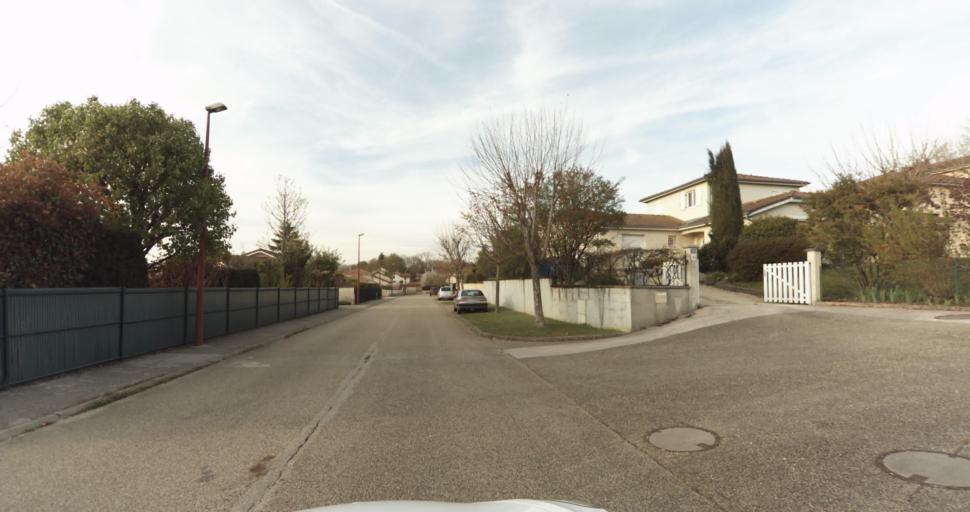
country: FR
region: Rhone-Alpes
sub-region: Departement de l'Ain
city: Amberieu-en-Bugey
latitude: 45.9660
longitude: 5.3590
